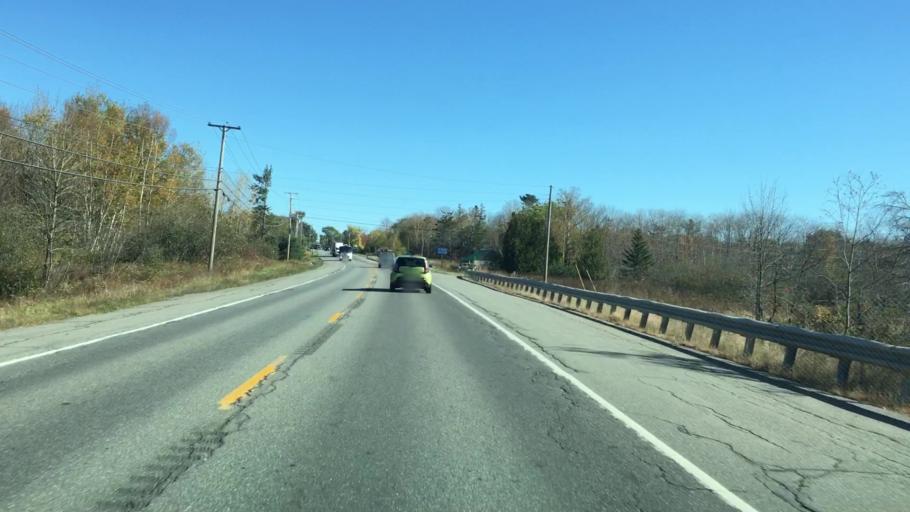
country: US
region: Maine
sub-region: Waldo County
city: Stockton Springs
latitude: 44.4708
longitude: -68.8935
